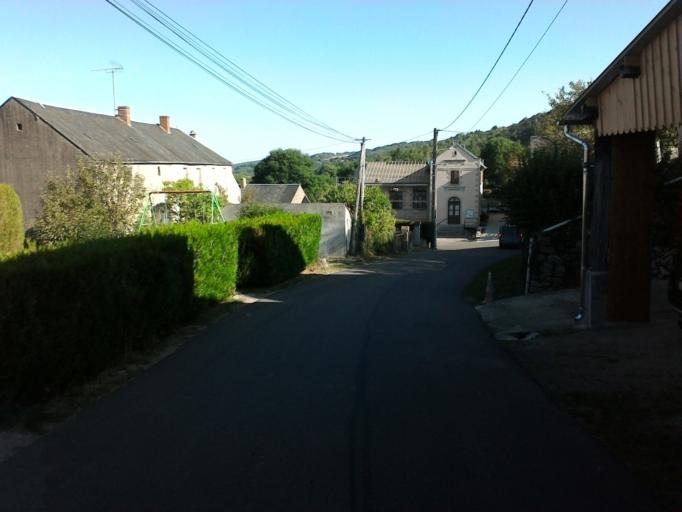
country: FR
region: Bourgogne
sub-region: Departement de la Nievre
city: Lormes
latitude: 47.3384
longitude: 3.9109
